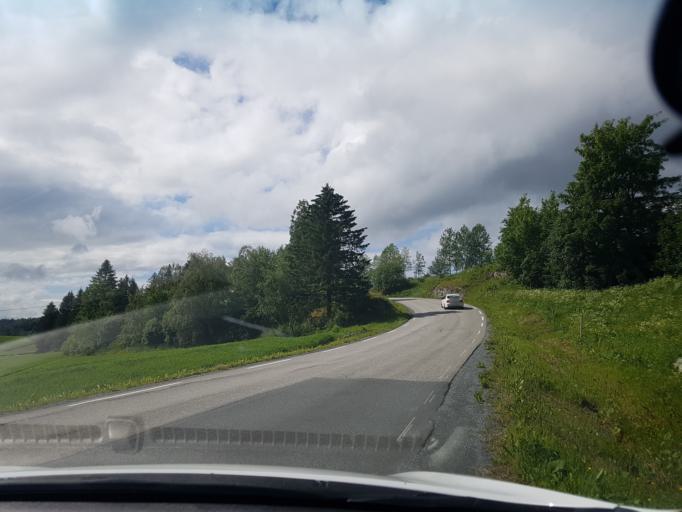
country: NO
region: Nord-Trondelag
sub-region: Stjordal
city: Stjordalshalsen
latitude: 63.5919
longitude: 10.9870
